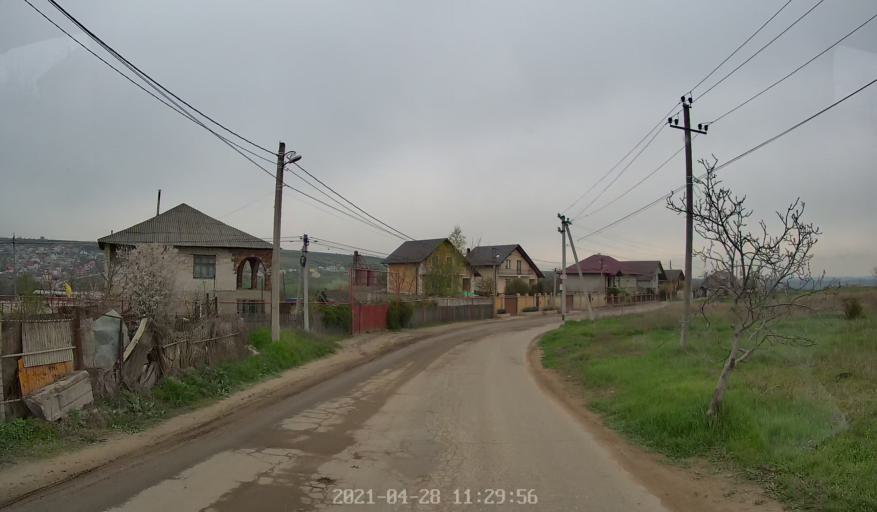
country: MD
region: Chisinau
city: Singera
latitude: 46.9778
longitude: 28.9351
